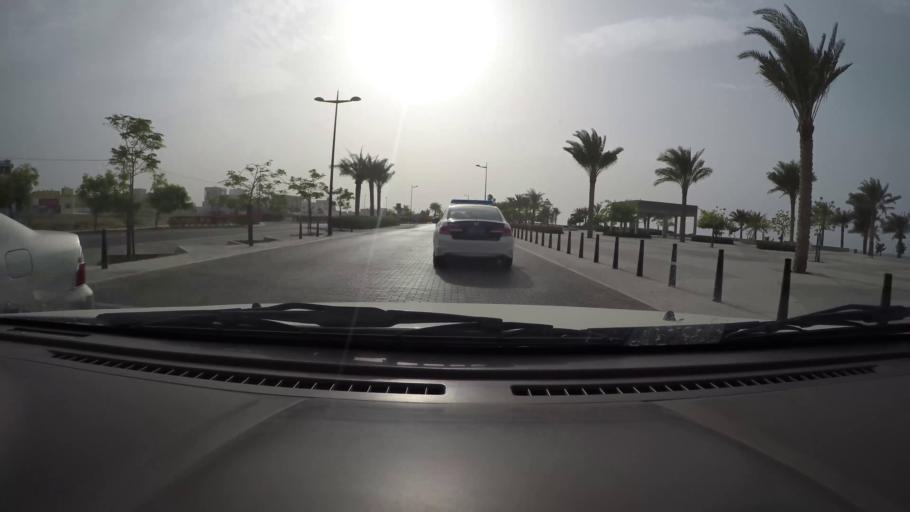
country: OM
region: Muhafazat Masqat
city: As Sib al Jadidah
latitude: 23.6964
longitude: 58.1520
